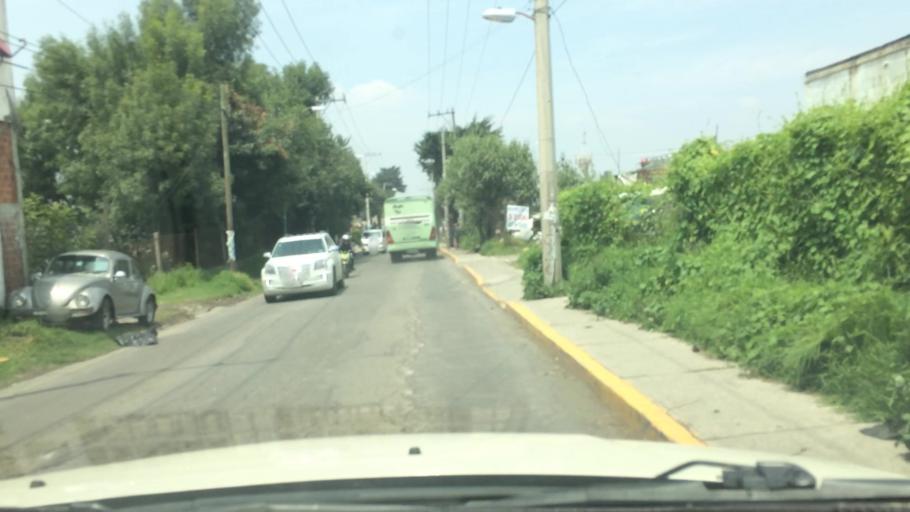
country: MX
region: Mexico City
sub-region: Tlalpan
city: Lomas de Tepemecatl
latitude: 19.2312
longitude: -99.1935
